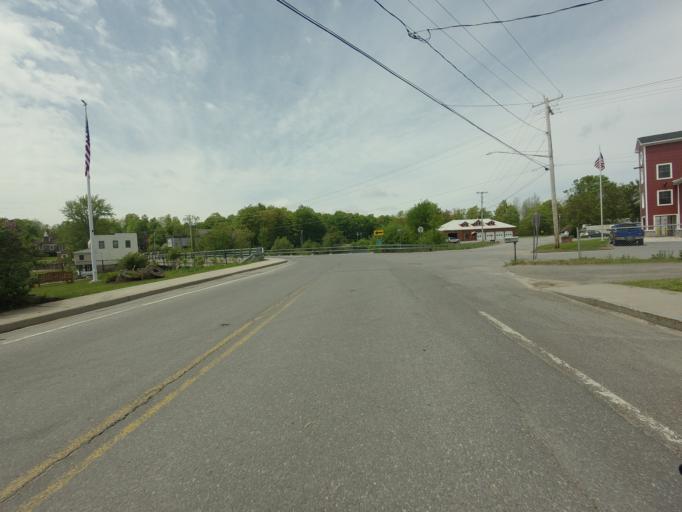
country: US
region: New York
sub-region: St. Lawrence County
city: Hannawa Falls
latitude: 44.5542
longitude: -74.9369
